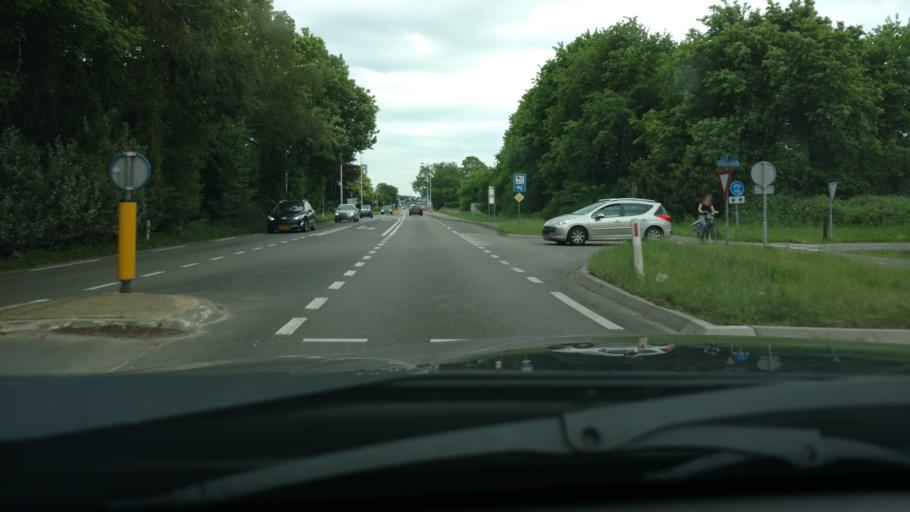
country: NL
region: Gelderland
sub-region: Gemeente Lochem
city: Epse
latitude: 52.2304
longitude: 6.1877
